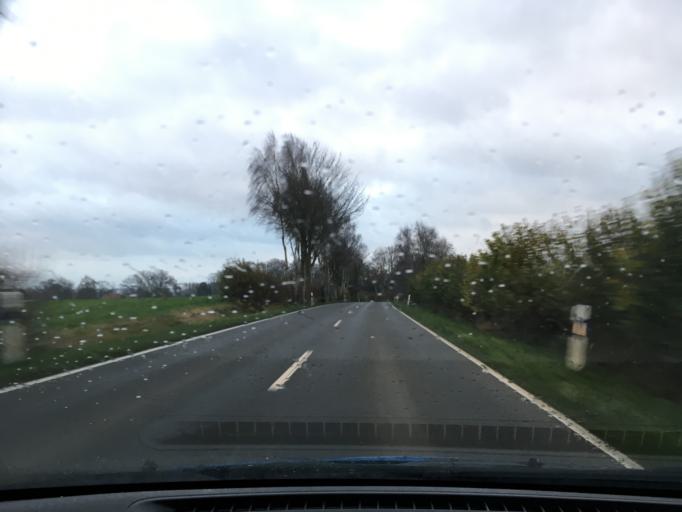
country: DE
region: Lower Saxony
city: Hermannsburg
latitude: 52.8205
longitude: 10.0580
